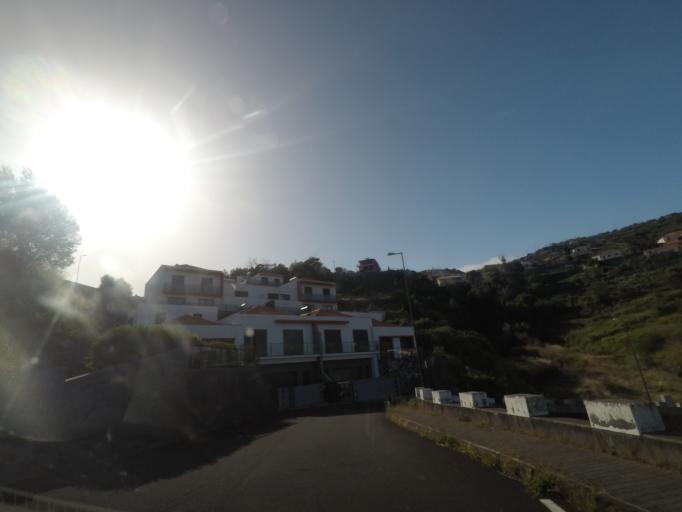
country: PT
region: Madeira
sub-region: Santa Cruz
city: Santa Cruz
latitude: 32.6907
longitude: -16.7930
